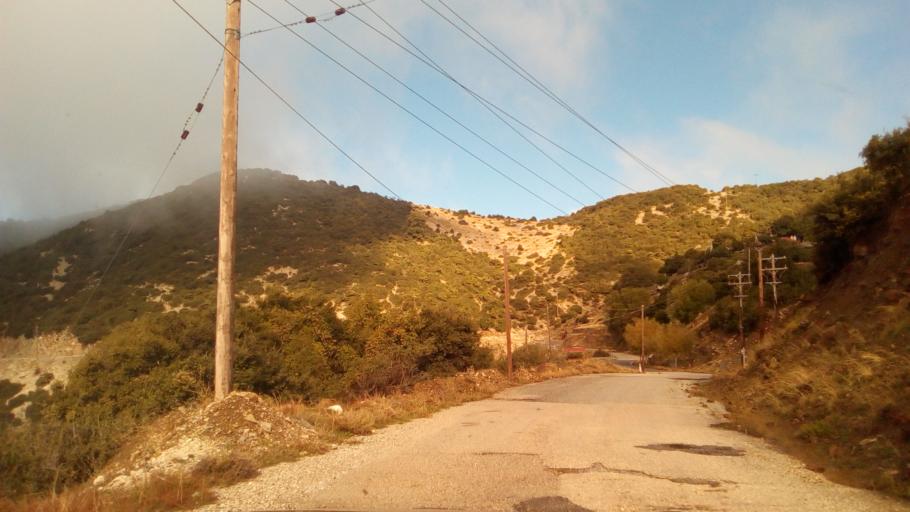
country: GR
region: West Greece
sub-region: Nomos Aitolias kai Akarnanias
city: Thermo
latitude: 38.5861
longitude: 21.7723
